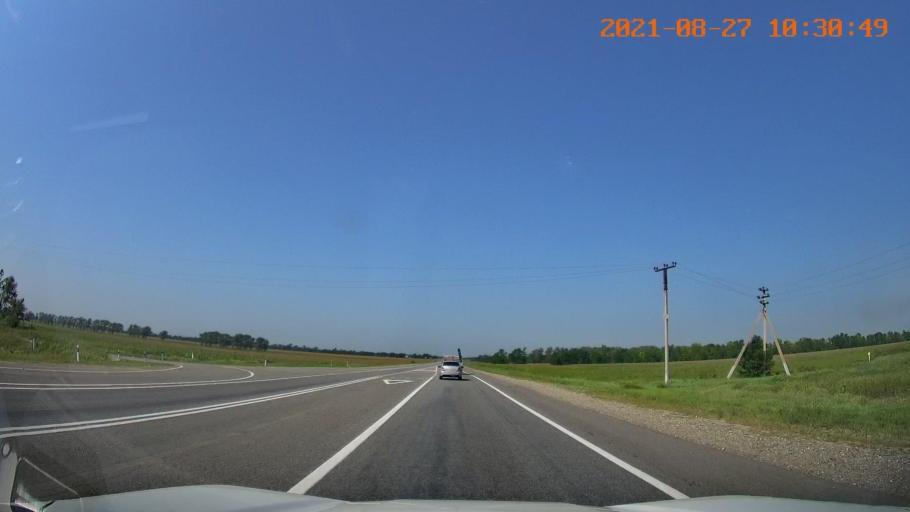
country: RU
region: Karachayevo-Cherkesiya
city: Kavkazskiy
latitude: 44.2628
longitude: 42.1729
